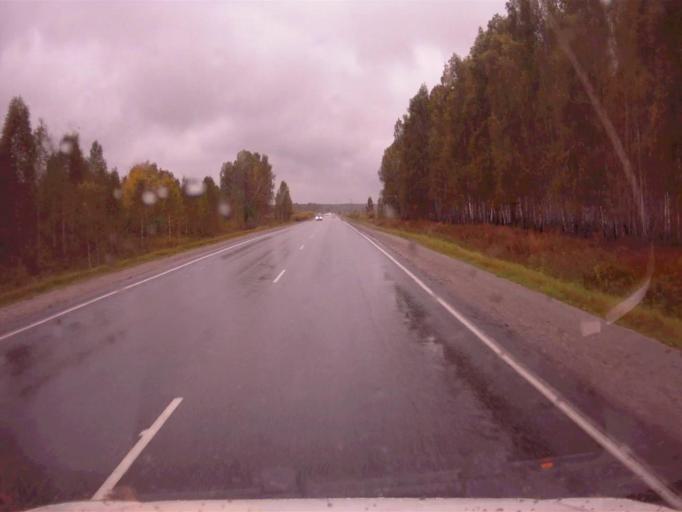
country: RU
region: Chelyabinsk
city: Argayash
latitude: 55.4789
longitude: 60.8216
